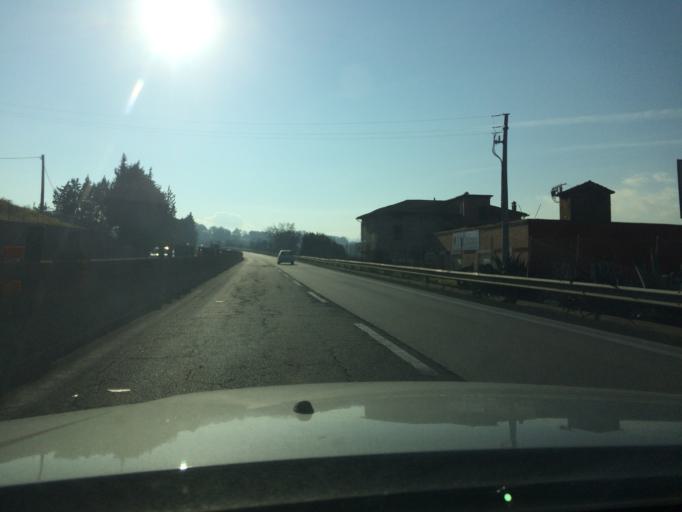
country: IT
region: Umbria
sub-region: Provincia di Perugia
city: Ponterio-Pian di Porto
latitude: 42.8332
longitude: 12.4015
